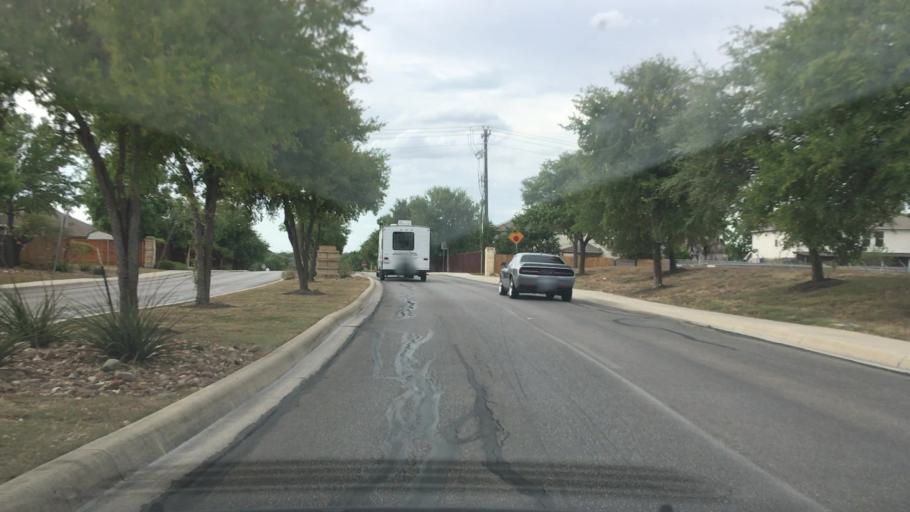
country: US
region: Texas
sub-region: Guadalupe County
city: Cibolo
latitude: 29.5839
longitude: -98.2467
